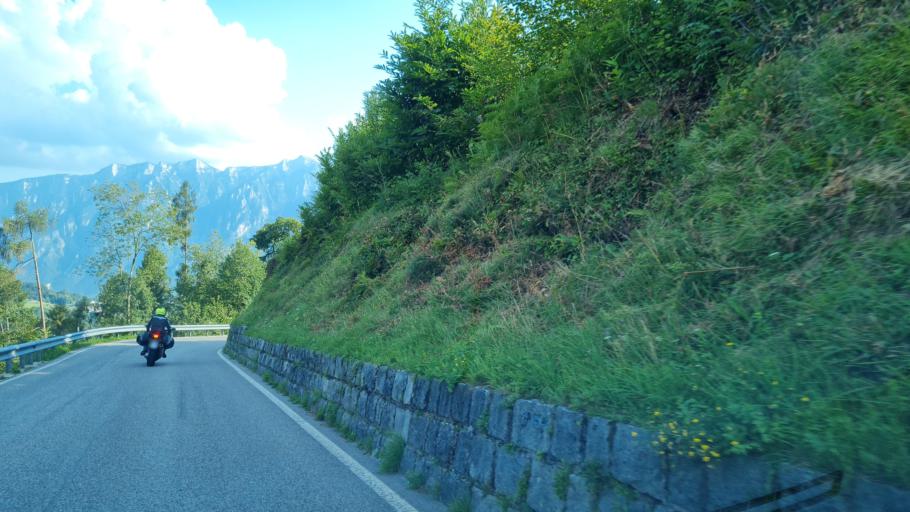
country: IT
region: Trentino-Alto Adige
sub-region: Provincia di Trento
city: Carzano
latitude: 46.0927
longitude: 11.4983
